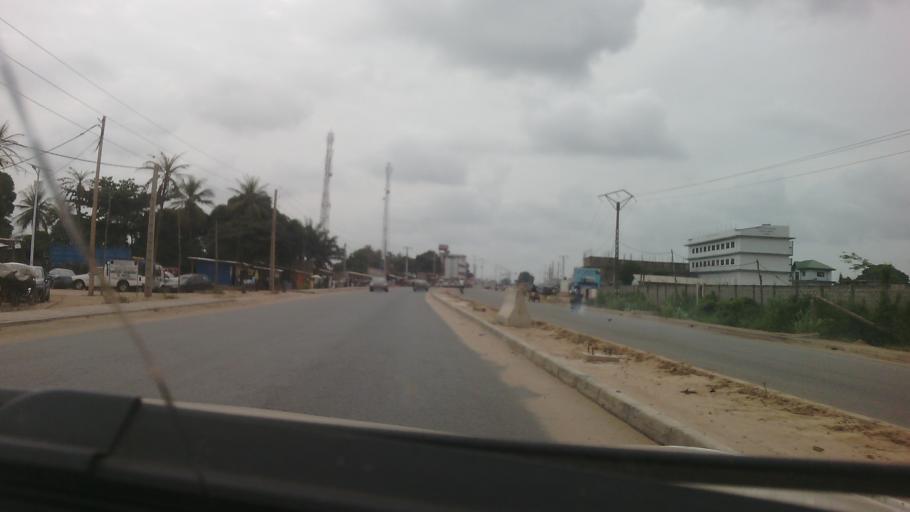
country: BJ
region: Atlantique
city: Hevie
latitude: 6.3853
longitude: 2.2065
